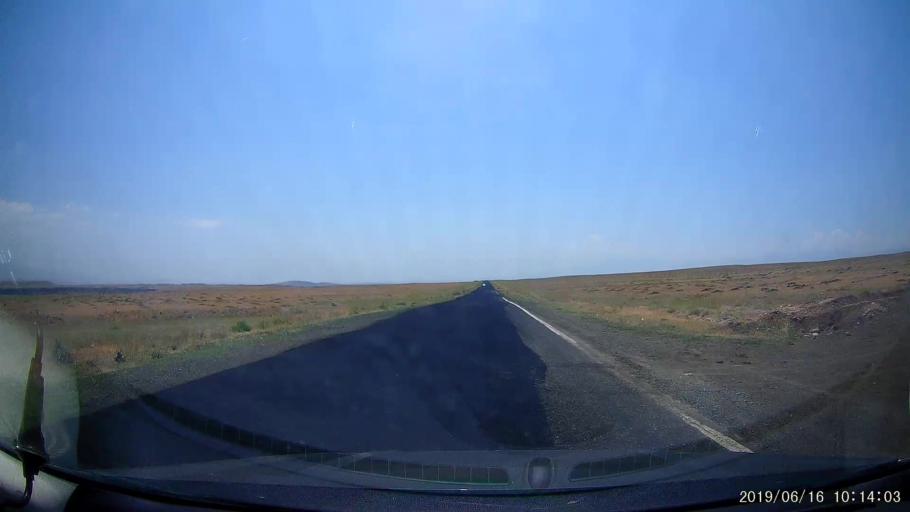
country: TR
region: Igdir
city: Tuzluca
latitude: 40.1882
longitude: 43.6548
